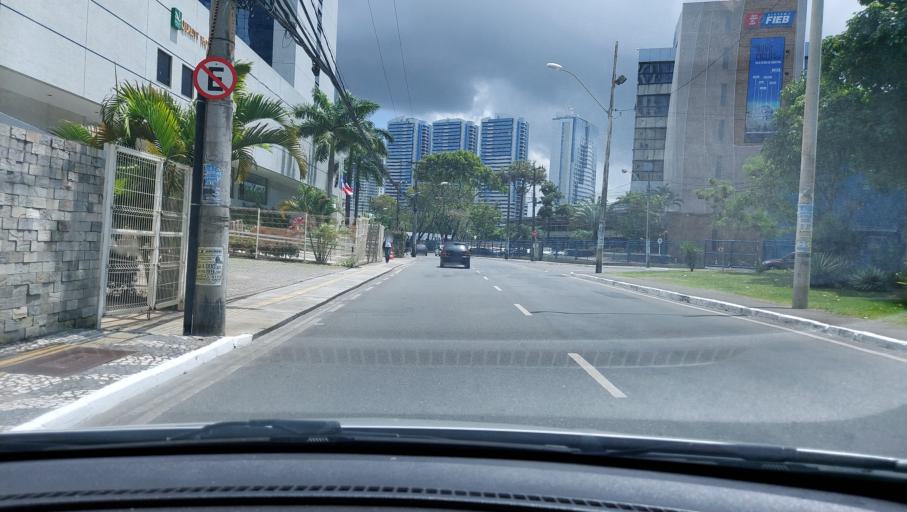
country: BR
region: Bahia
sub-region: Salvador
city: Salvador
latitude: -12.9853
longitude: -38.4490
